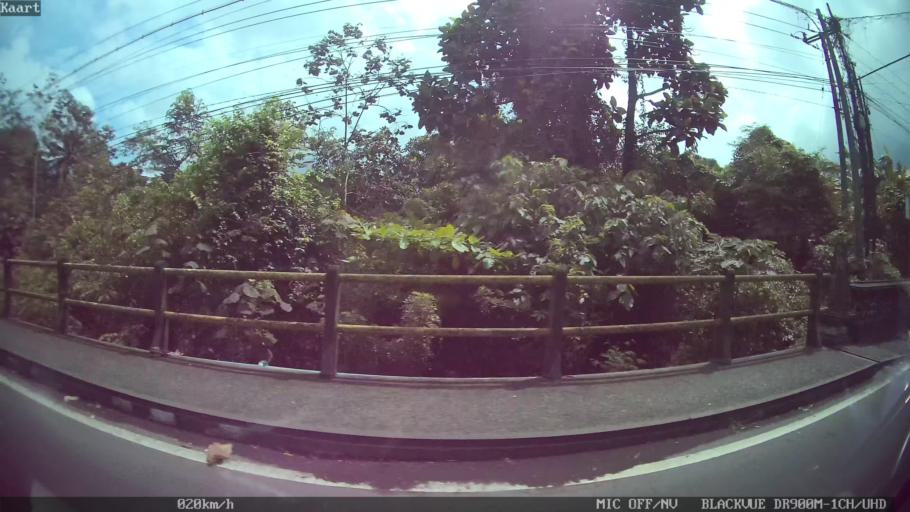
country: ID
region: Bali
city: Banjar Kelodan
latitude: -8.5369
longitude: 115.3328
